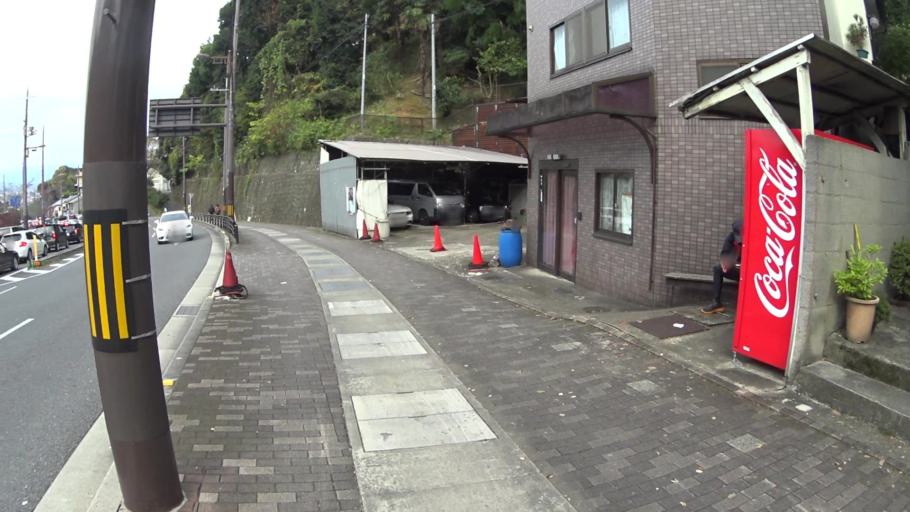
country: JP
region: Kyoto
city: Kyoto
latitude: 35.0053
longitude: 135.7892
